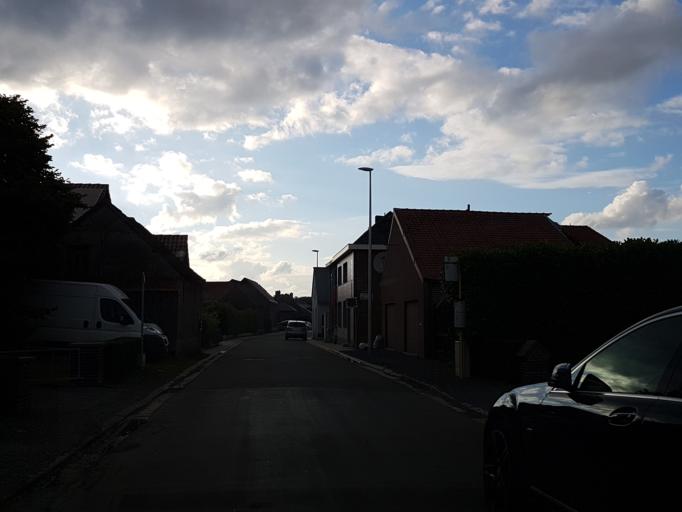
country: BE
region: Flanders
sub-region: Provincie Vlaams-Brabant
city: Opwijk
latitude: 50.9760
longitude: 4.1934
